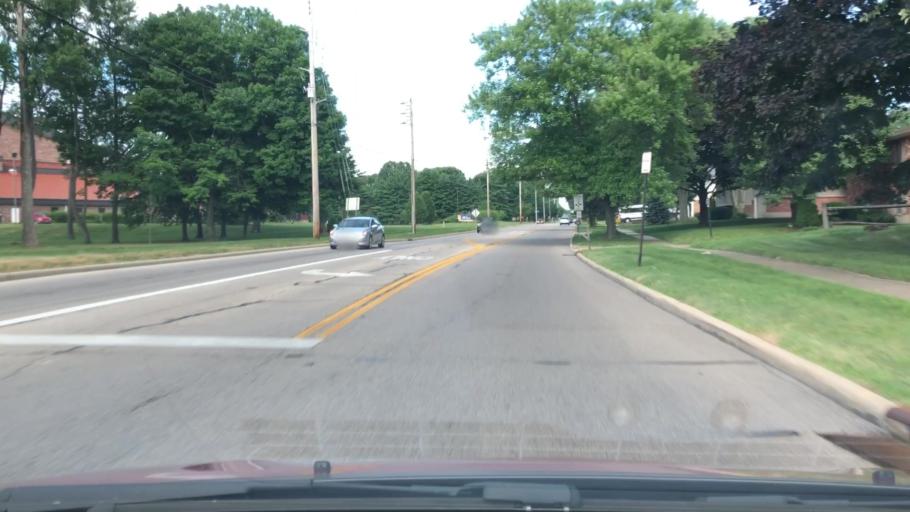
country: US
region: Ohio
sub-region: Montgomery County
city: Centerville
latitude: 39.6587
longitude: -84.1467
